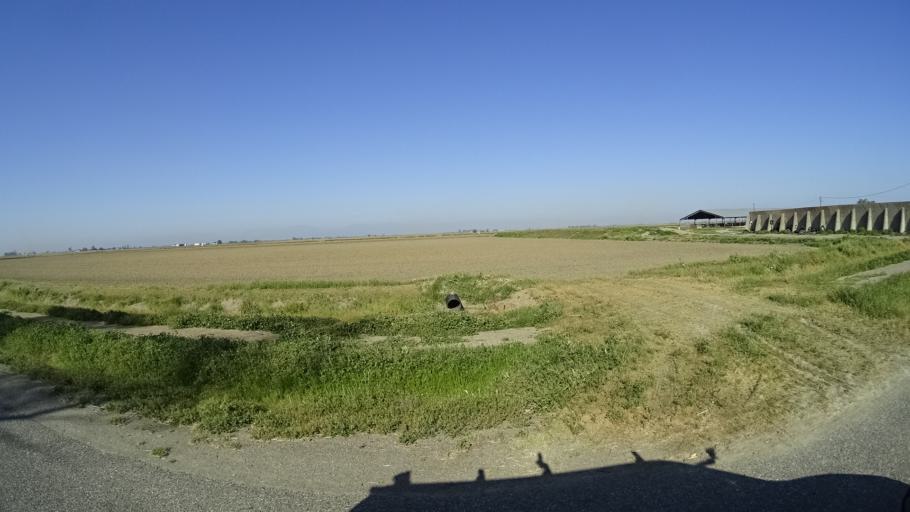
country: US
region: California
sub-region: Glenn County
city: Willows
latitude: 39.5499
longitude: -122.1026
